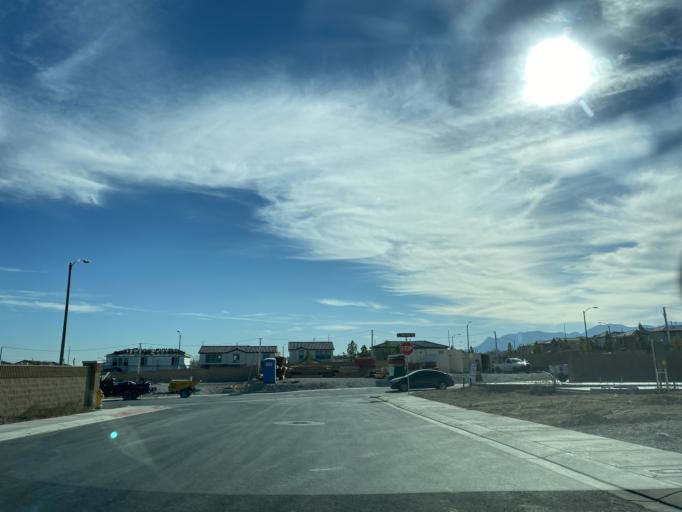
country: US
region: Nevada
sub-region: Clark County
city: Summerlin South
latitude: 36.3115
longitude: -115.3207
